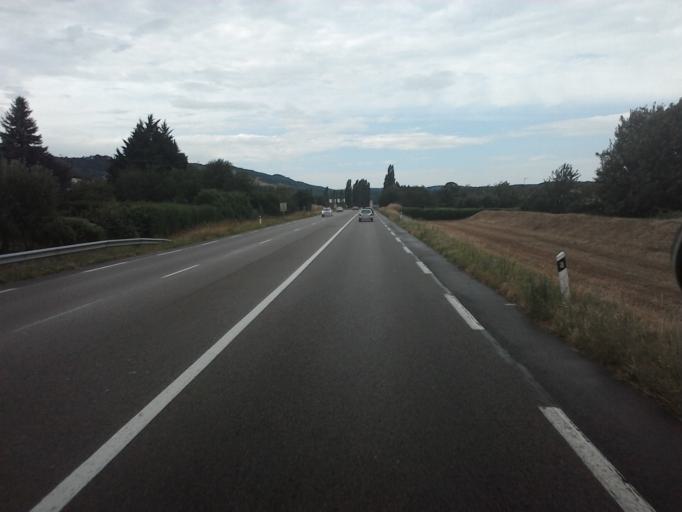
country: FR
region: Franche-Comte
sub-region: Departement du Jura
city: Poligny
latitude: 46.8417
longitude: 5.6999
